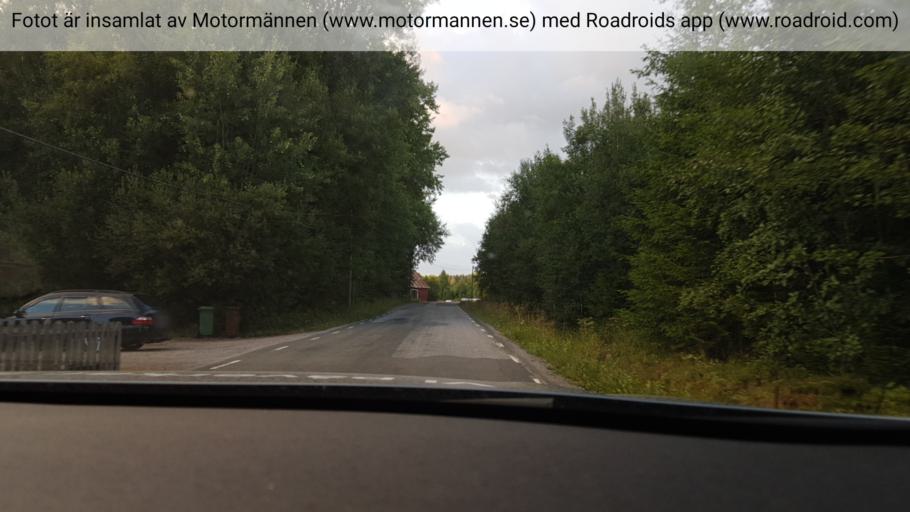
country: SE
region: Vaestra Goetaland
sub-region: Falkopings Kommun
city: Floby
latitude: 58.0742
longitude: 13.3976
